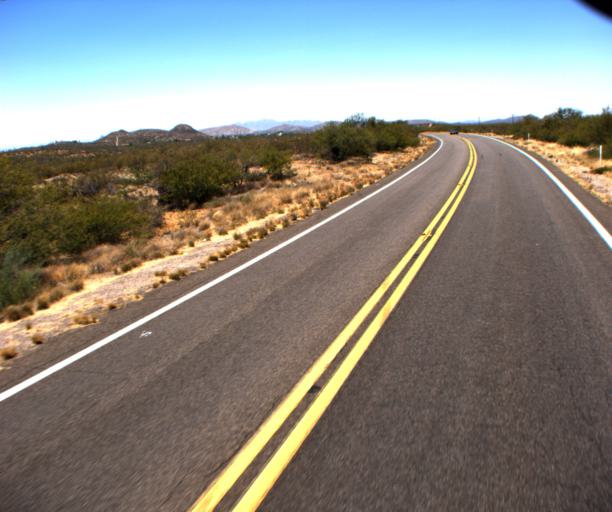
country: US
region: Arizona
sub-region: Pima County
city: Catalina
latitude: 32.6459
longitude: -111.0205
